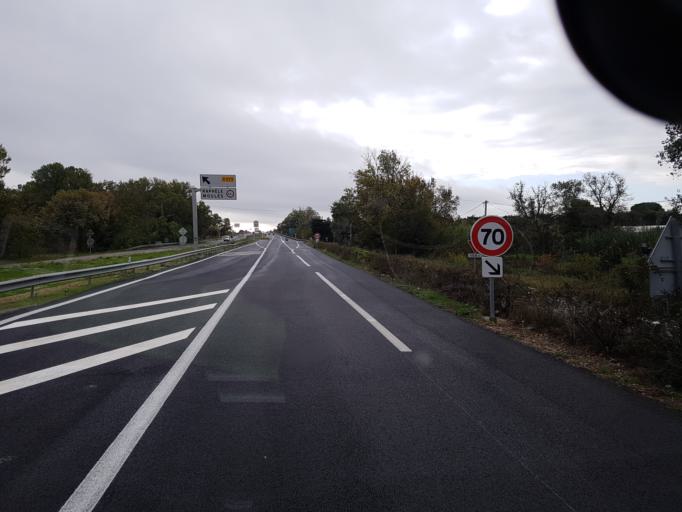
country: FR
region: Provence-Alpes-Cote d'Azur
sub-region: Departement des Bouches-du-Rhone
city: Saint-Martin-de-Crau
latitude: 43.6276
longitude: 4.7476
